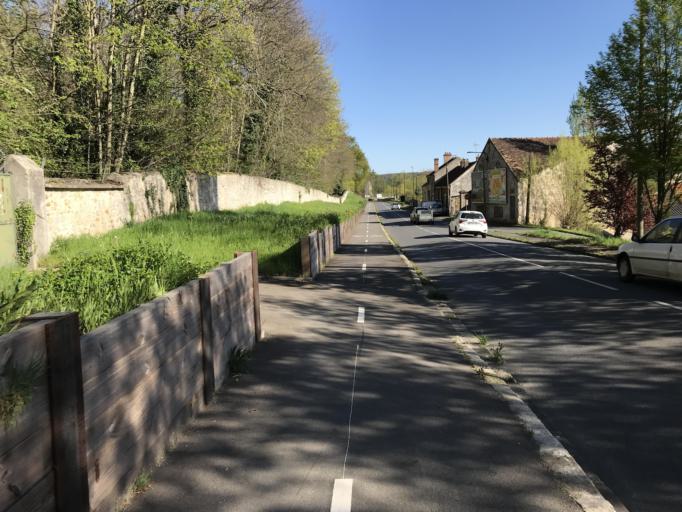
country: FR
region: Ile-de-France
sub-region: Departement de l'Essonne
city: Marcoussis
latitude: 48.6489
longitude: 2.2175
